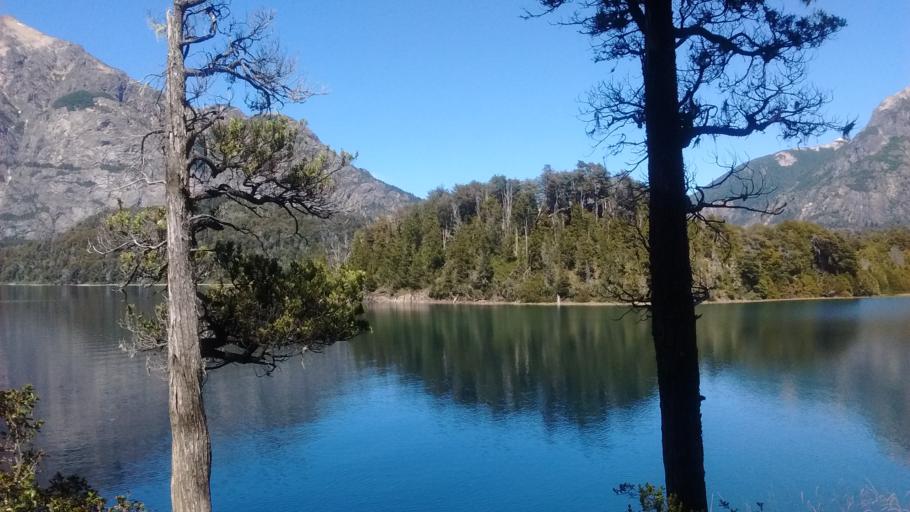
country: AR
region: Rio Negro
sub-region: Departamento de Bariloche
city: San Carlos de Bariloche
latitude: -41.0555
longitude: -71.5561
